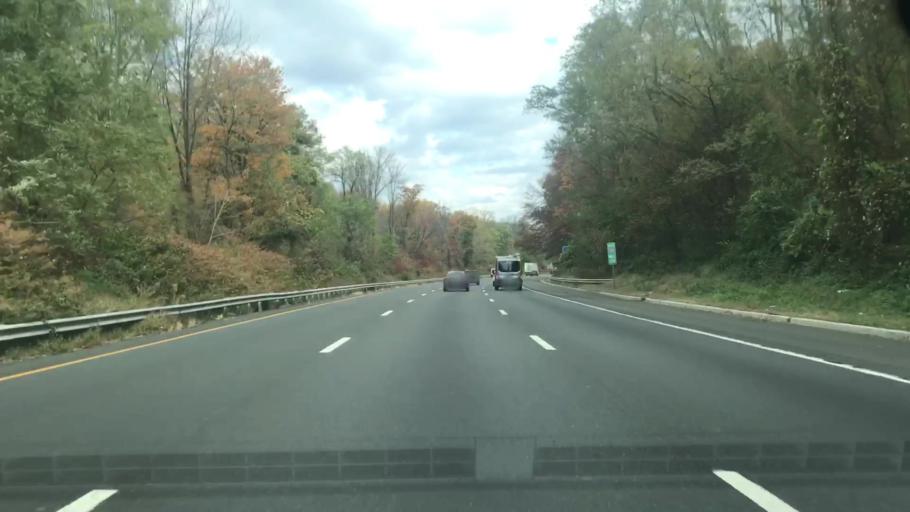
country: US
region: New Jersey
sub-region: Somerset County
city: Bernardsville
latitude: 40.7557
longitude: -74.5241
